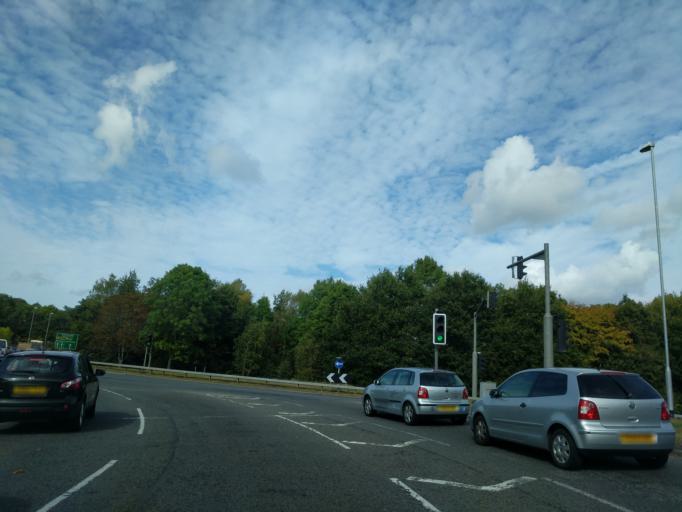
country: GB
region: England
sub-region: Northamptonshire
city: Hardingstone
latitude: 52.2139
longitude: -0.8932
